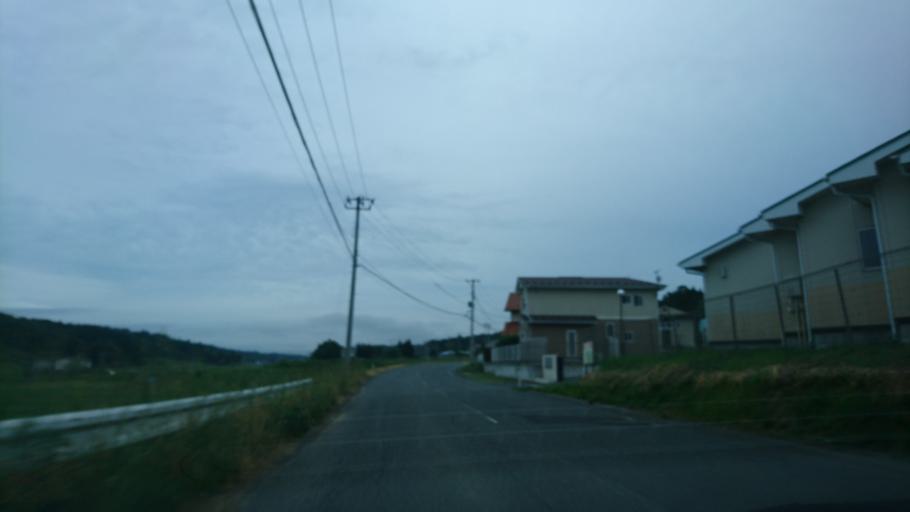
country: JP
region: Iwate
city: Ichinoseki
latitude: 38.9298
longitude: 141.1725
